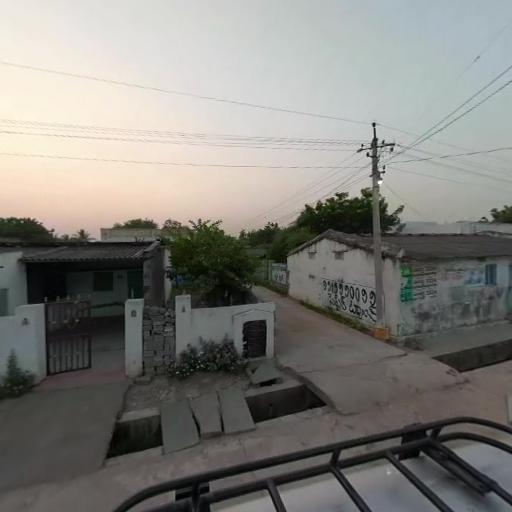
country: IN
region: Telangana
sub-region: Nalgonda
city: Suriapet
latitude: 17.1065
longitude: 79.5283
